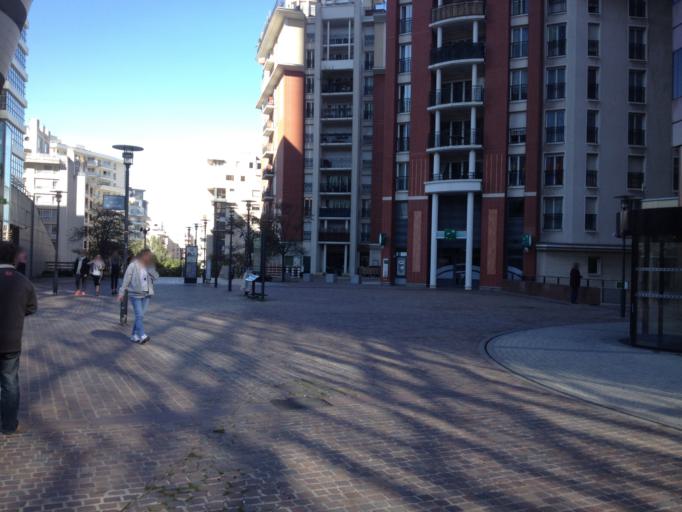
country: FR
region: Ile-de-France
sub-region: Departement des Hauts-de-Seine
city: La Defense
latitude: 48.8957
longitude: 2.2373
